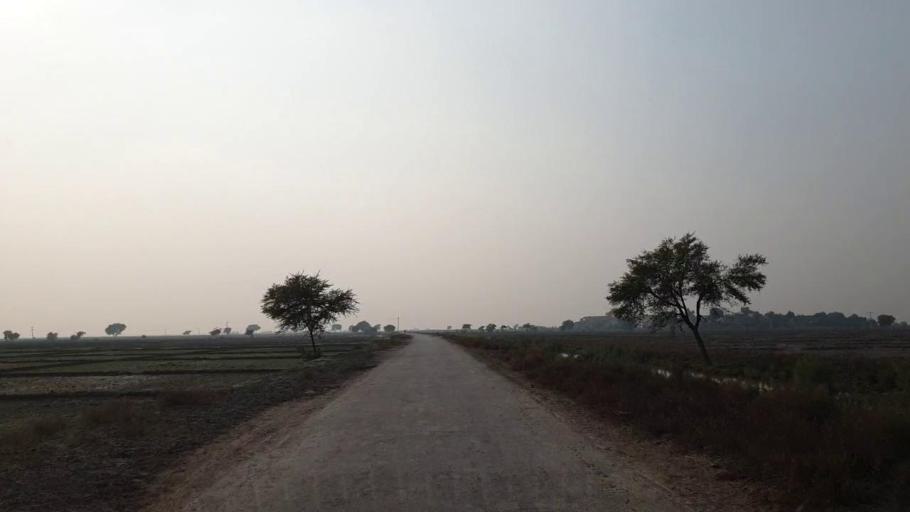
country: PK
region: Sindh
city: Bhan
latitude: 26.4881
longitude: 67.7094
